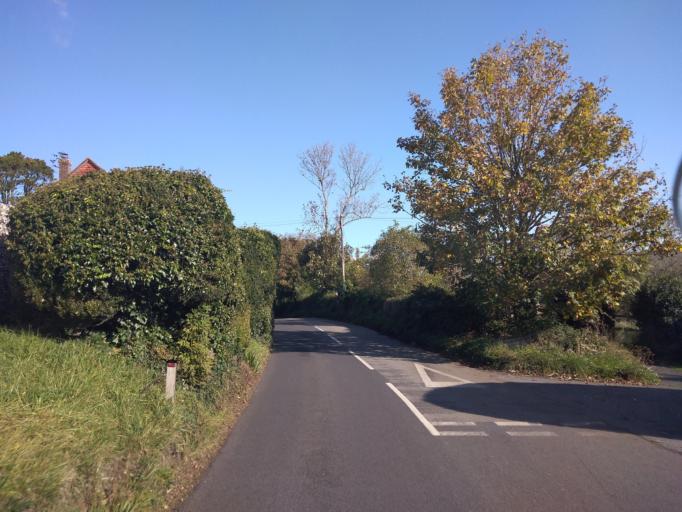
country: GB
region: England
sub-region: East Sussex
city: Seaford
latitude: 50.7974
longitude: 0.1523
